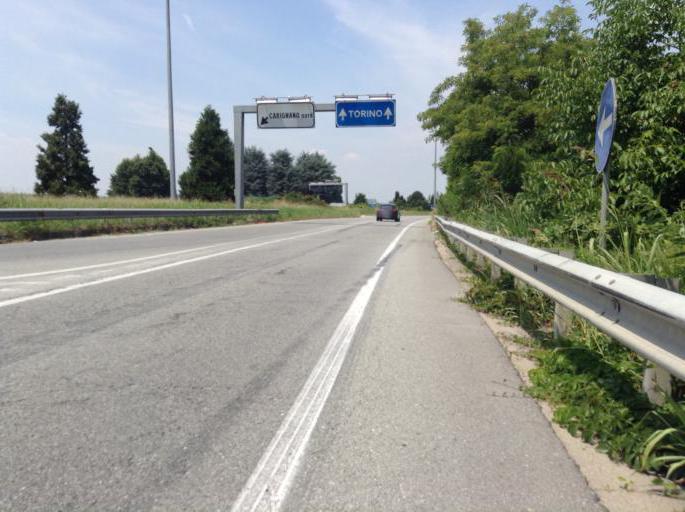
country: IT
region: Piedmont
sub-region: Provincia di Torino
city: Carignano
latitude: 44.9164
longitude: 7.6766
